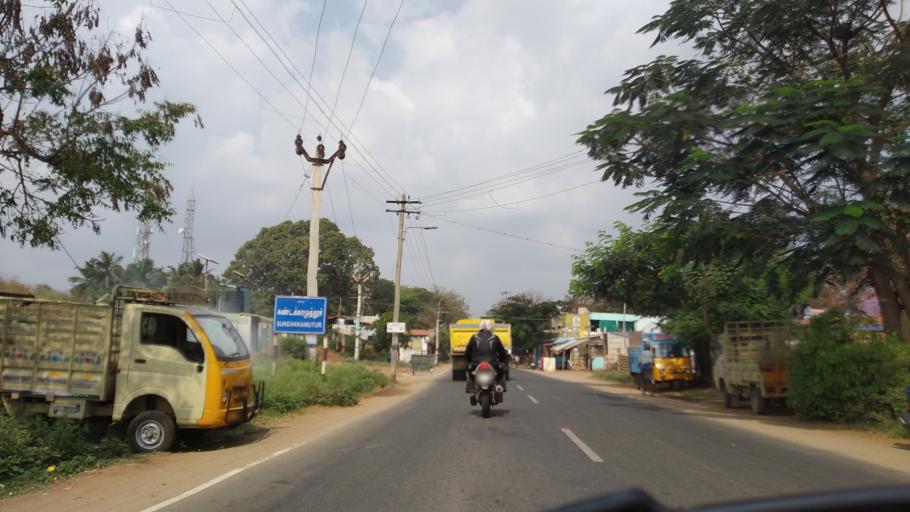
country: IN
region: Tamil Nadu
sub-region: Coimbatore
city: Perur
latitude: 10.9563
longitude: 76.9261
